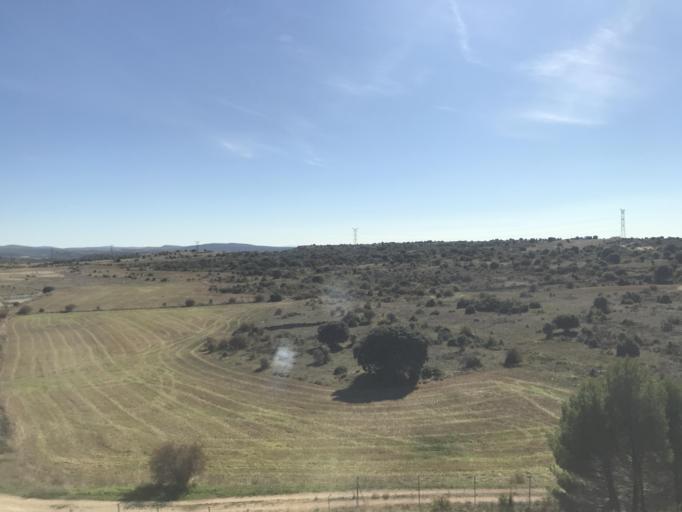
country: ES
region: Castille-La Mancha
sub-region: Provincia de Guadalajara
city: Alcolea del Pinar
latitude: 41.0344
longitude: -2.4519
